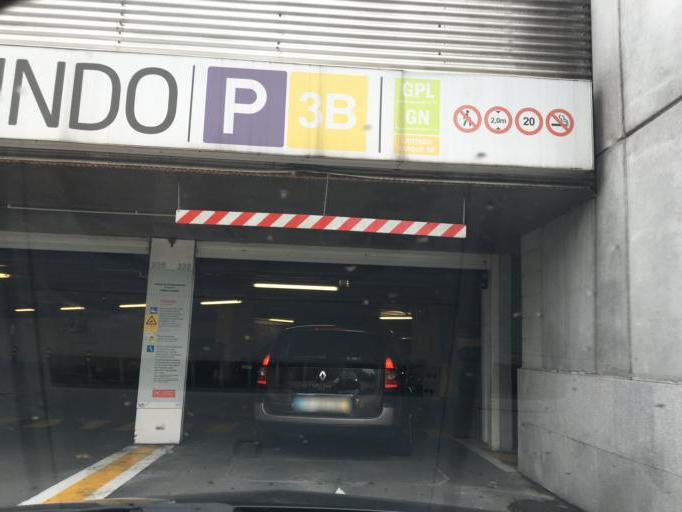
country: PT
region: Porto
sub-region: Maia
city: Pedroucos
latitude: 41.1643
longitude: -8.5845
